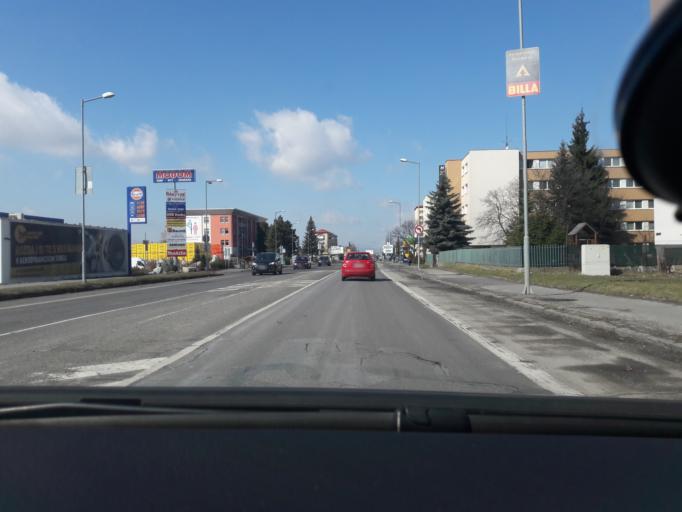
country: SK
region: Zilinsky
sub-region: Okres Liptovsky Mikulas
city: Liptovsky Mikulas
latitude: 49.0788
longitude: 19.6343
